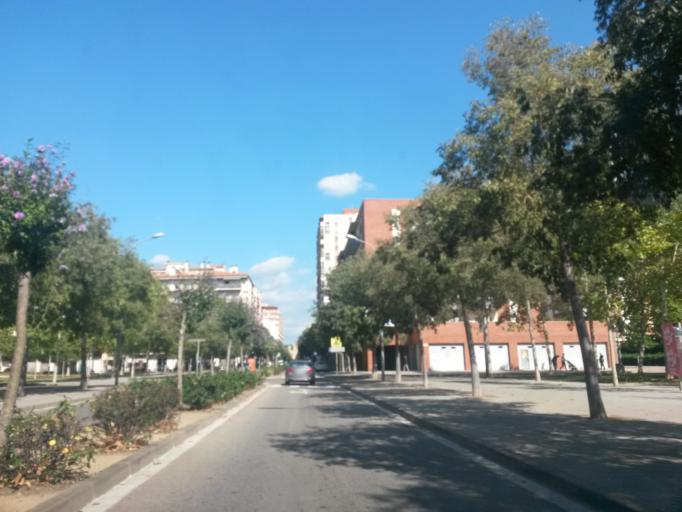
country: ES
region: Catalonia
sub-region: Provincia de Girona
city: Salt
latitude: 41.9709
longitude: 2.7924
